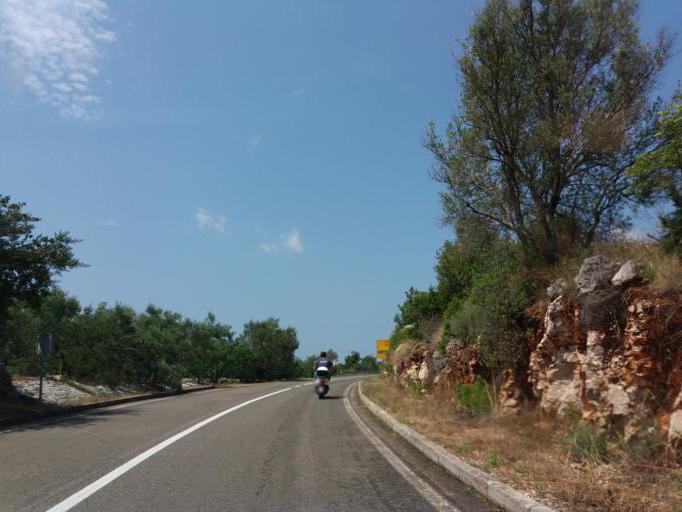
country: HR
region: Zadarska
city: Sali
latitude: 43.9349
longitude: 15.1502
